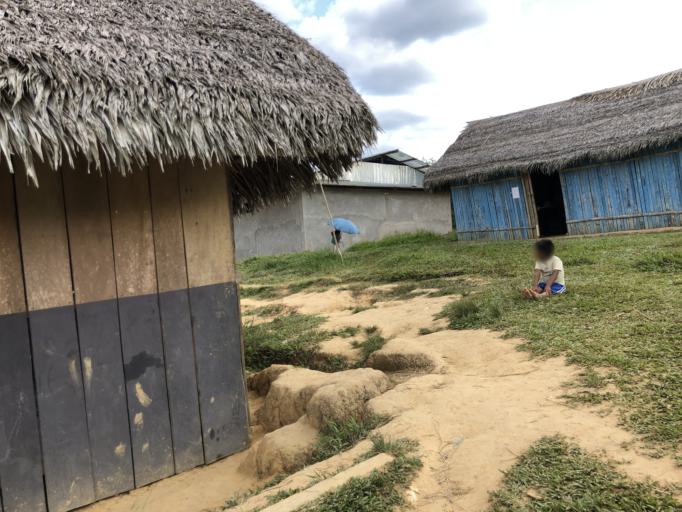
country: PE
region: Loreto
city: Puerto Galilea
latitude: -4.0587
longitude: -77.7602
